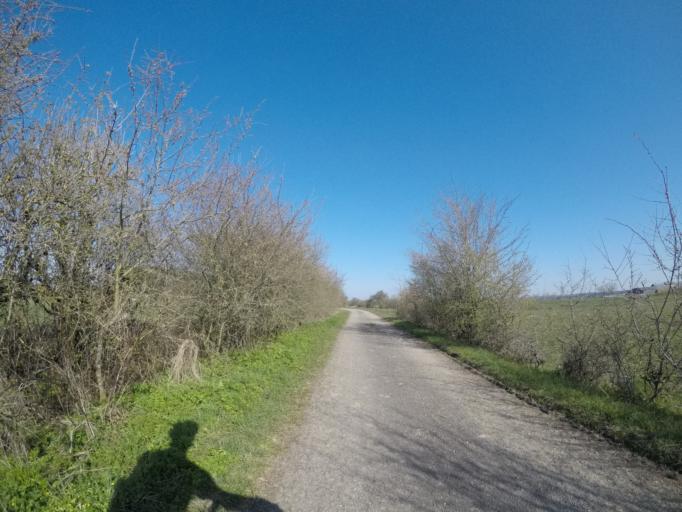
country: BE
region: Wallonia
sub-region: Province du Luxembourg
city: Etalle
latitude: 49.7102
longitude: 5.5770
